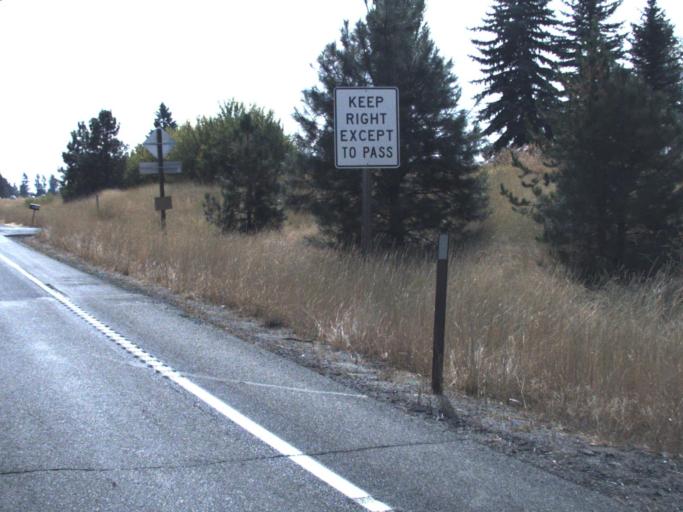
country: US
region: Washington
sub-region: Spokane County
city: Deer Park
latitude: 47.8839
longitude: -117.4230
